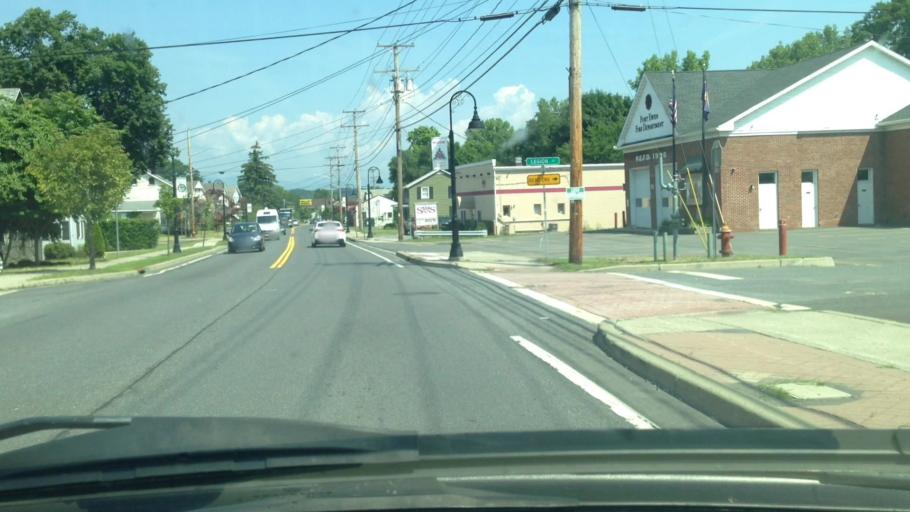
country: US
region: New York
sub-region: Ulster County
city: Port Ewen
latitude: 41.9077
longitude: -73.9769
